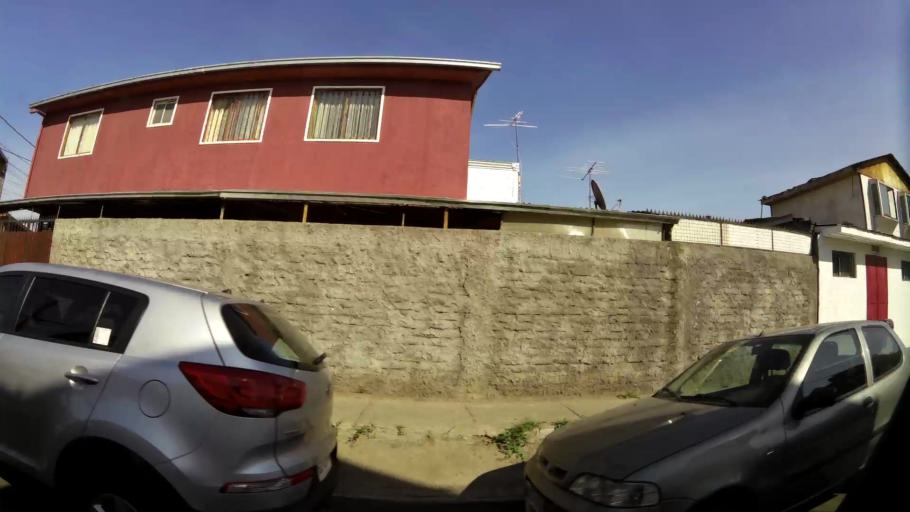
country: CL
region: Santiago Metropolitan
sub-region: Provincia de Santiago
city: Lo Prado
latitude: -33.4162
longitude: -70.7620
